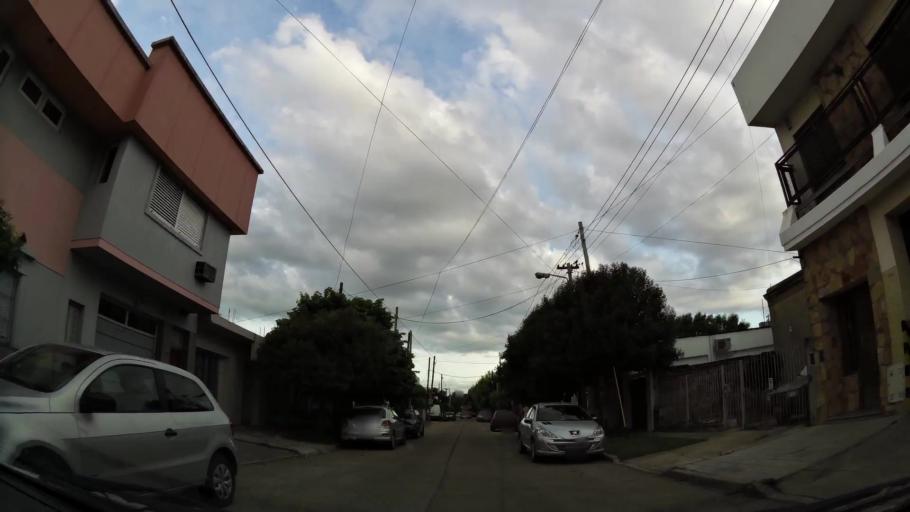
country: AR
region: Buenos Aires
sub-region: Partido de Quilmes
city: Quilmes
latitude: -34.7336
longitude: -58.2512
